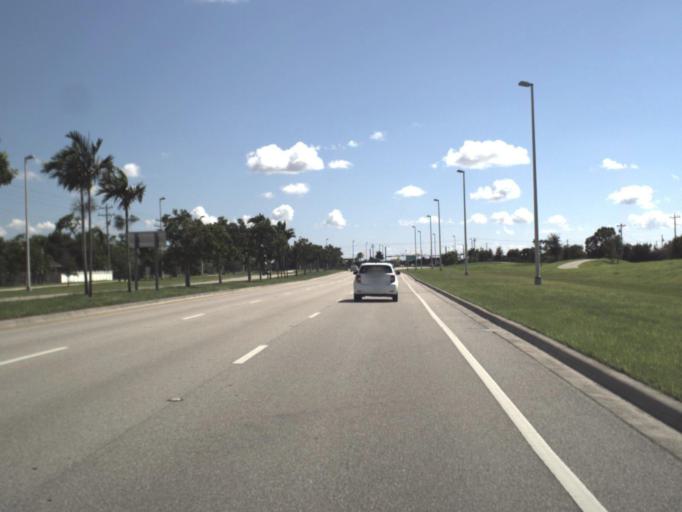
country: US
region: Florida
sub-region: Lee County
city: Palmona Park
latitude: 26.6882
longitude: -81.9418
